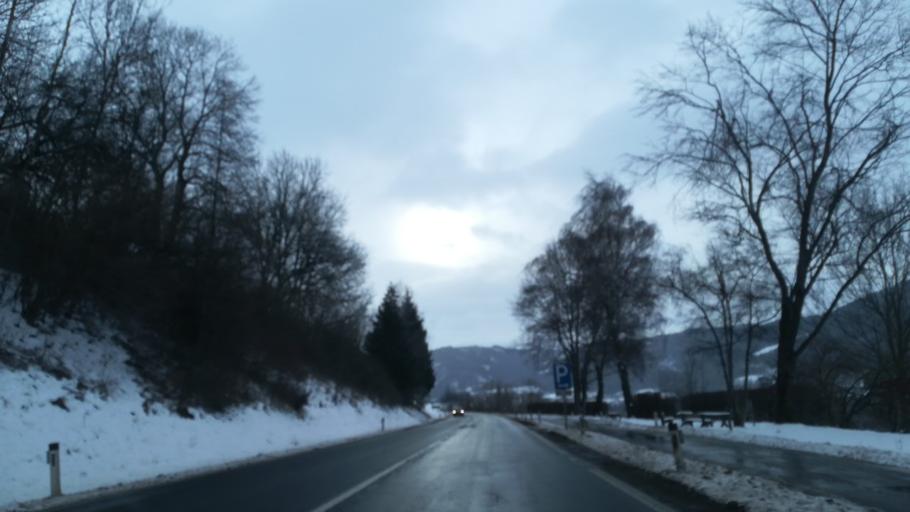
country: AT
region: Styria
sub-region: Politischer Bezirk Murtal
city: Poels
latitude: 47.2041
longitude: 14.5857
